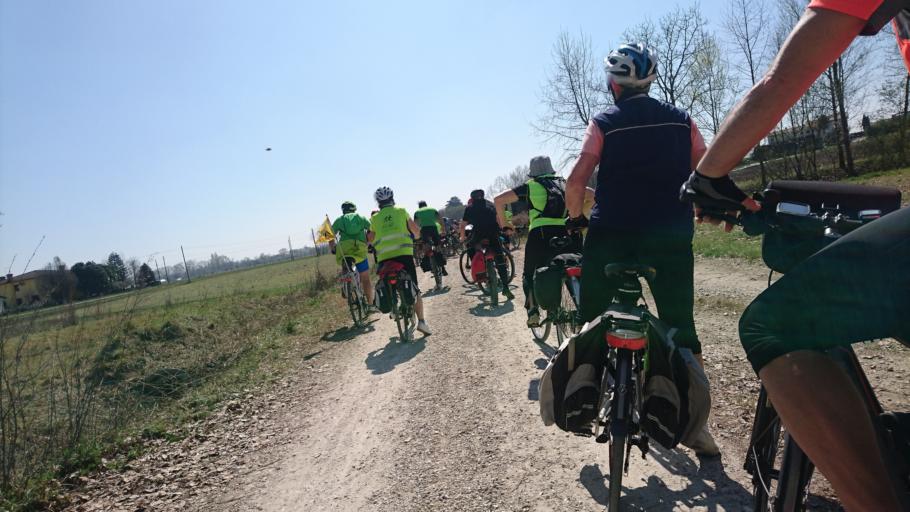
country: IT
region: Veneto
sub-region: Provincia di Padova
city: Piazzola sul Brenta
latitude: 45.5670
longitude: 11.7611
